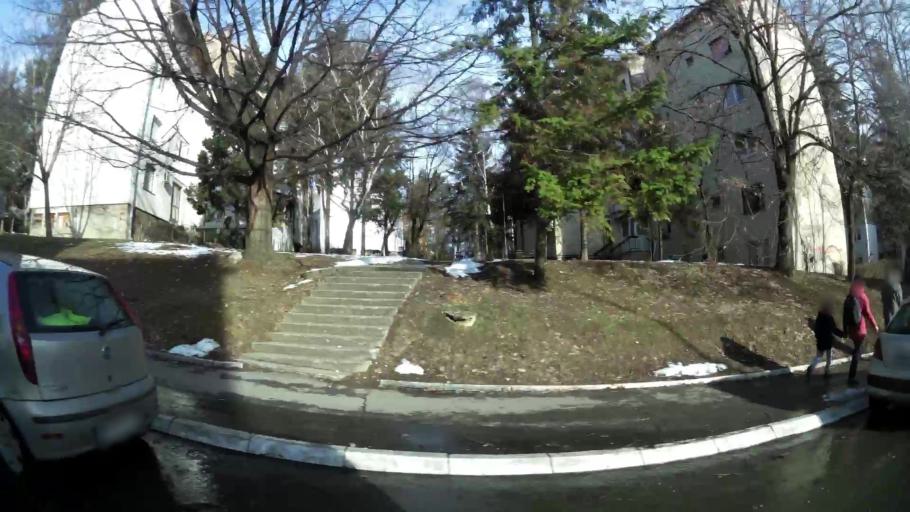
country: RS
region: Central Serbia
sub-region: Belgrade
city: Rakovica
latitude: 44.7242
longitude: 20.4279
